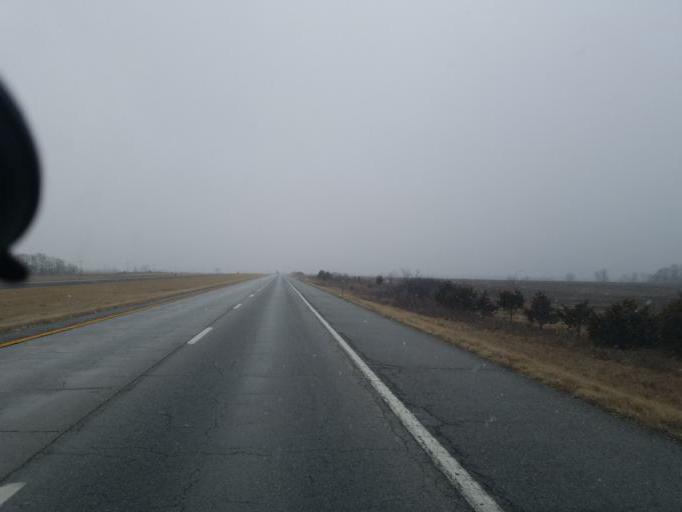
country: US
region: Missouri
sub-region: Macon County
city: La Plata
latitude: 39.9475
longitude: -92.4771
